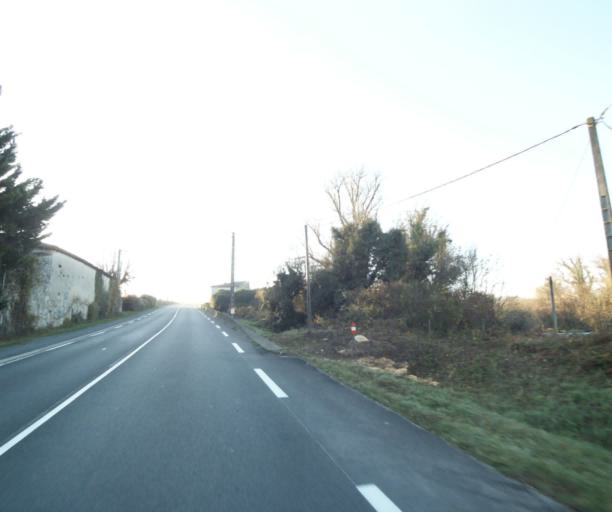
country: FR
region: Poitou-Charentes
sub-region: Departement de la Charente-Maritime
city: Cherac
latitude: 45.7182
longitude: -0.4947
